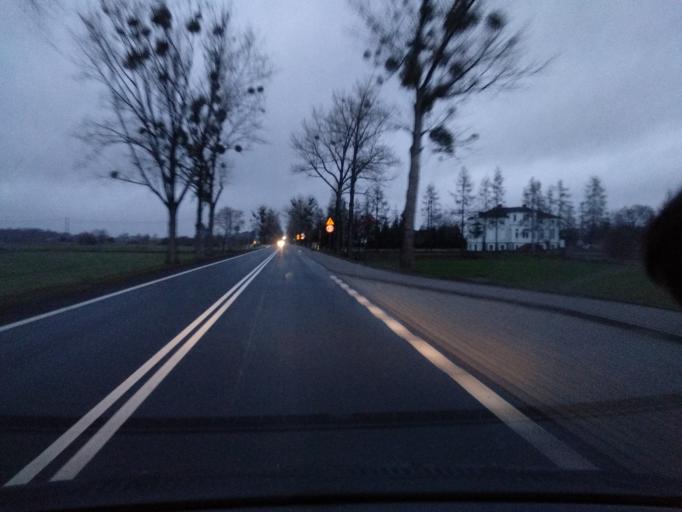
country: PL
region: Lower Silesian Voivodeship
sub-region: Powiat sredzki
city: Malczyce
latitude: 51.1837
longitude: 16.5213
